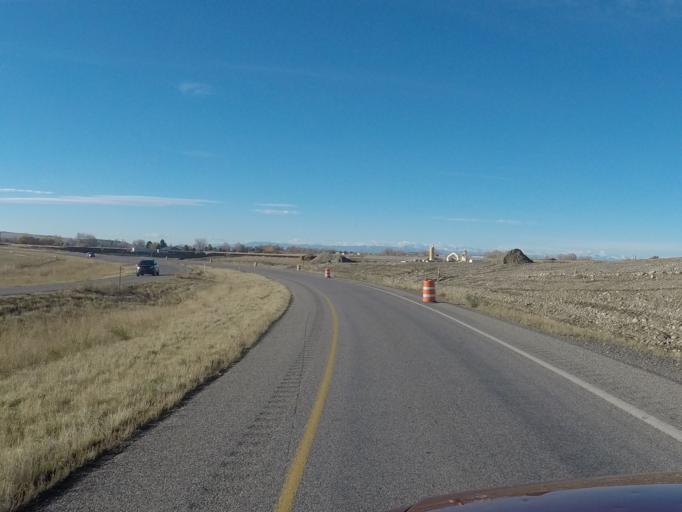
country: US
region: Montana
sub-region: Yellowstone County
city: Laurel
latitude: 45.6402
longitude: -108.7659
